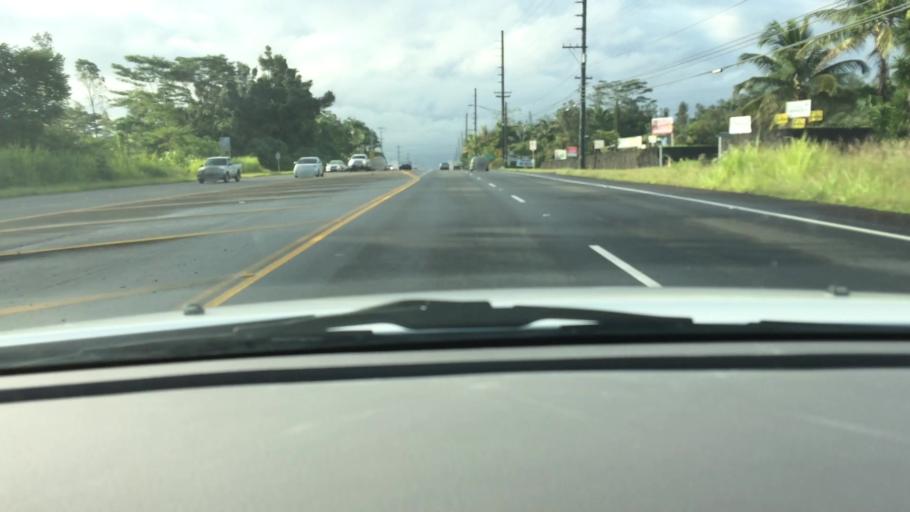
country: US
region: Hawaii
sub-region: Hawaii County
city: Kea'au
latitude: 19.6064
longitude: -155.0279
